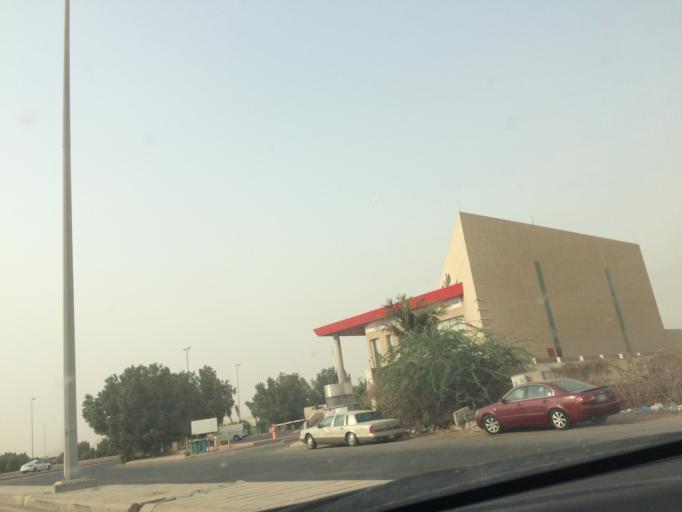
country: SA
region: Makkah
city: Jeddah
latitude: 21.4961
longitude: 39.2185
